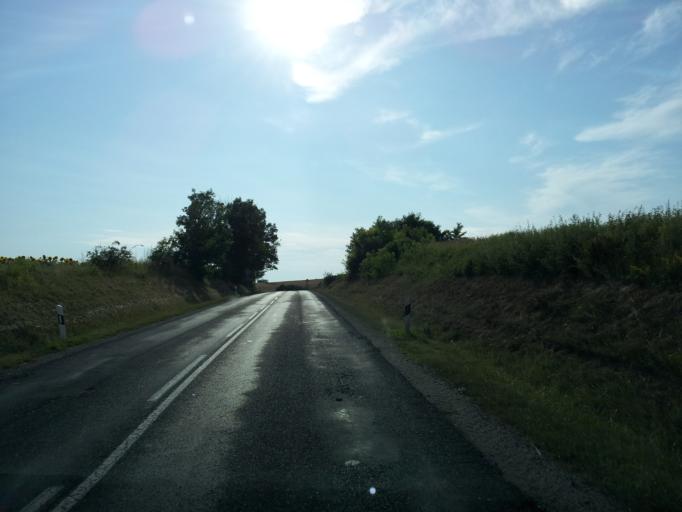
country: HU
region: Veszprem
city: Urkut
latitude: 46.9911
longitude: 17.6789
